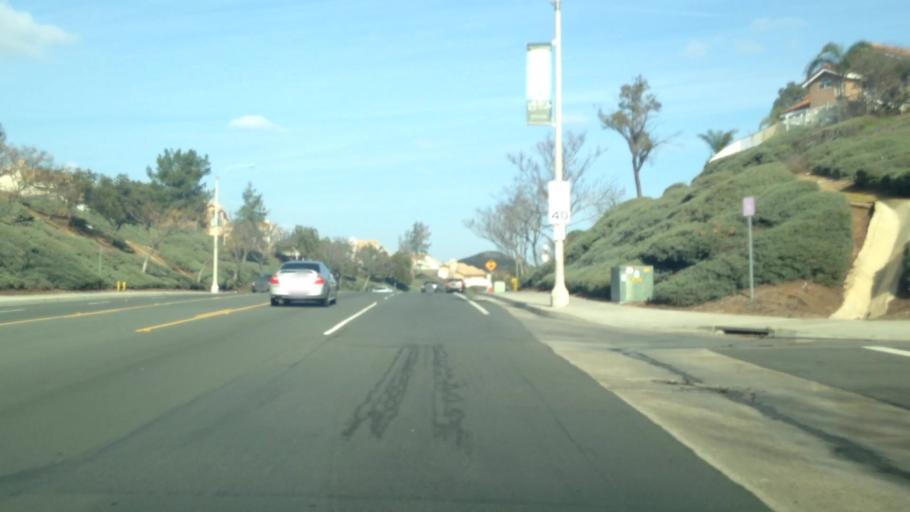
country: US
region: California
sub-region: Riverside County
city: Home Gardens
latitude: 33.8959
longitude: -117.5133
